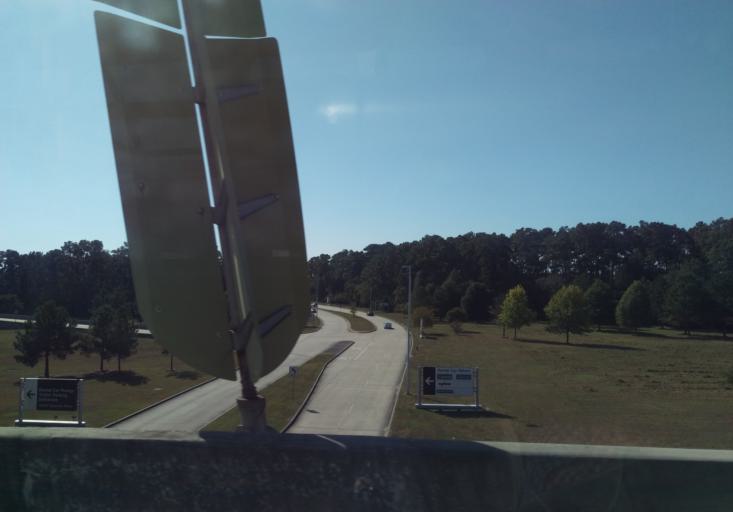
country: US
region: Texas
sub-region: Harris County
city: Aldine
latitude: 29.9696
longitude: -95.3357
